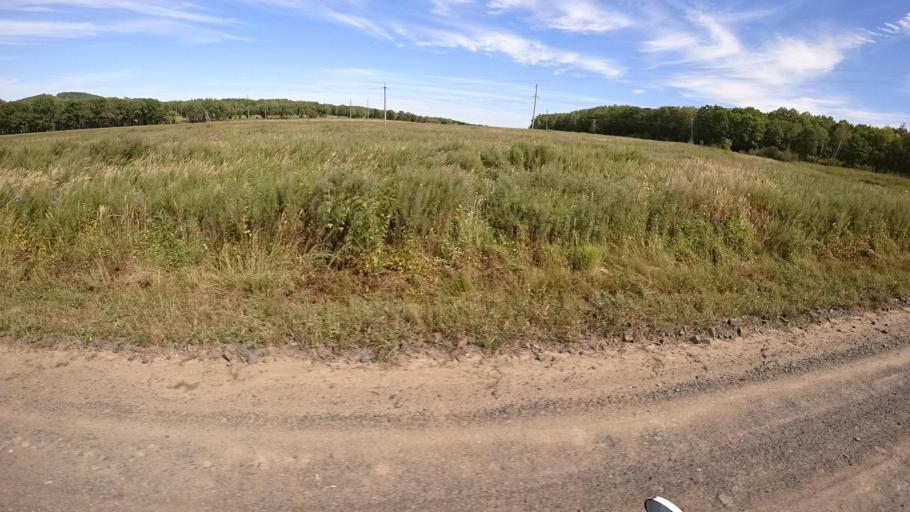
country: RU
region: Primorskiy
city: Yakovlevka
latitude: 44.7116
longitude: 133.6221
